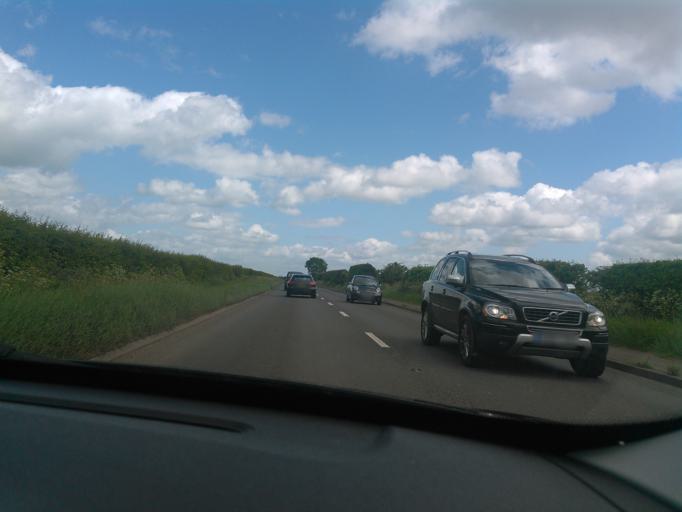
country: GB
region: England
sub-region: Shropshire
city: Stoke upon Tern
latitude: 52.8872
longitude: -2.5402
